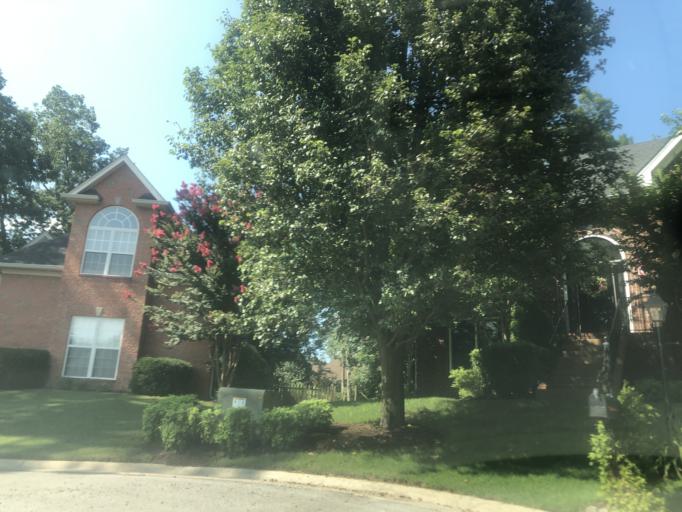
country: US
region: Tennessee
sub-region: Wilson County
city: Green Hill
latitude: 36.1524
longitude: -86.5924
